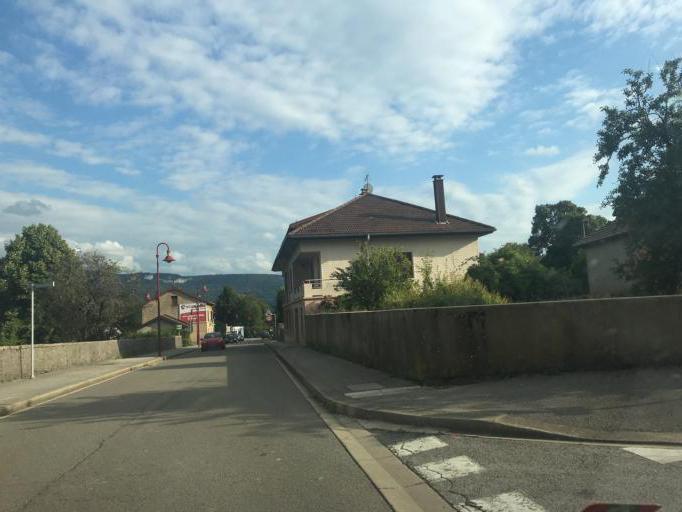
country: FR
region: Franche-Comte
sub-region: Departement du Jura
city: Saint-Lupicin
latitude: 46.3964
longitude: 5.7941
